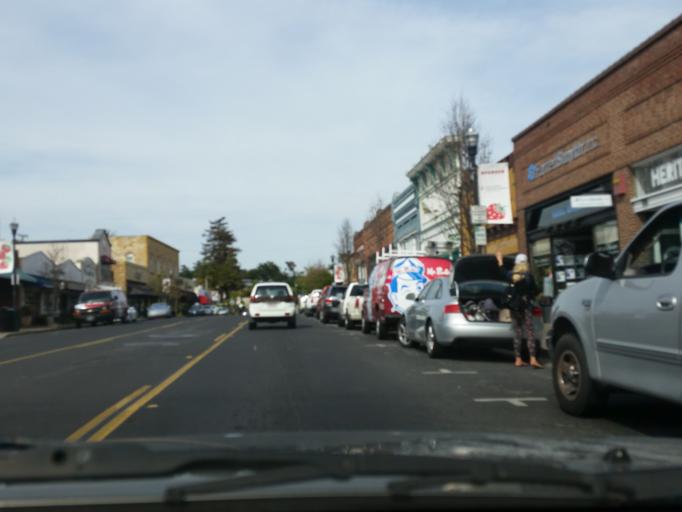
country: US
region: California
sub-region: San Luis Obispo County
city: Arroyo Grande
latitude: 35.1233
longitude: -120.5789
